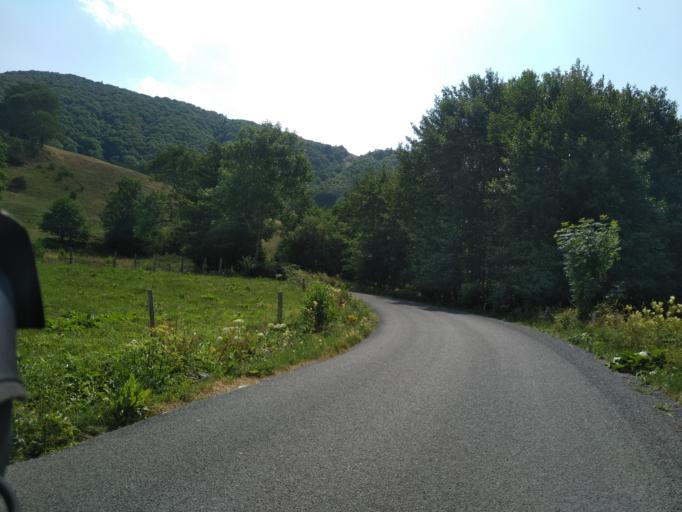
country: FR
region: Auvergne
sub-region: Departement du Cantal
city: Riom-es-Montagnes
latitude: 45.1383
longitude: 2.6974
